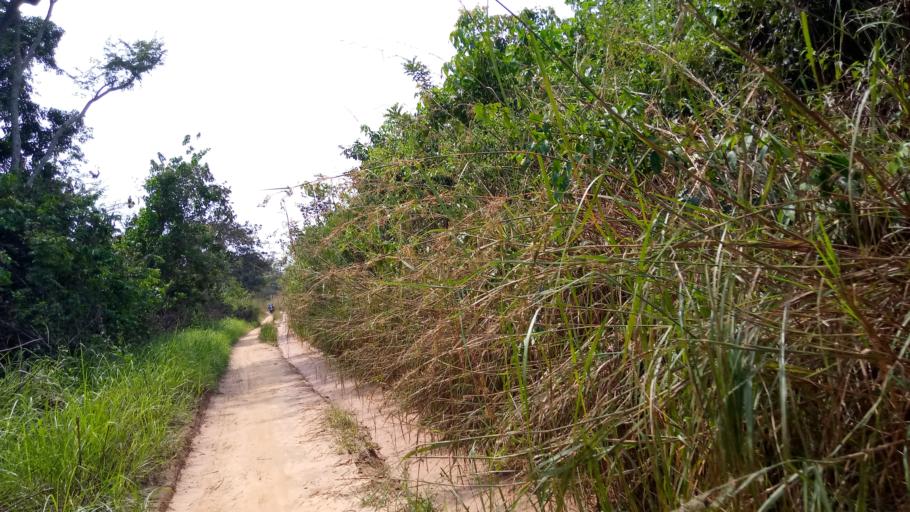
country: CD
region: Bandundu
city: Bandundu
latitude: -4.1498
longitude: 17.4147
